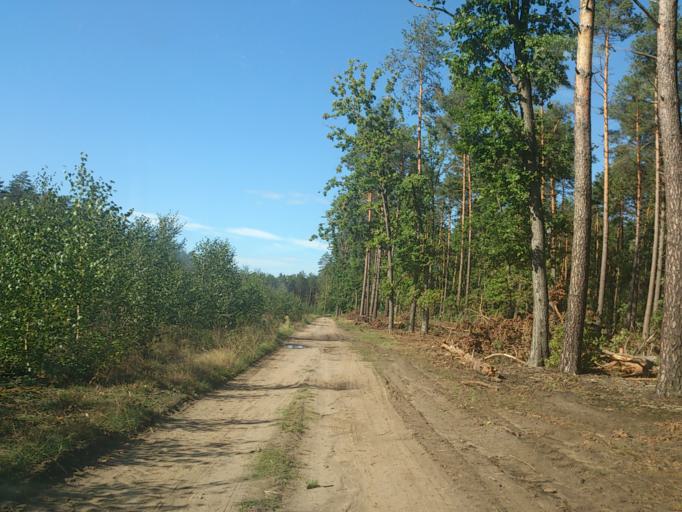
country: PL
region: Kujawsko-Pomorskie
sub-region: Powiat golubsko-dobrzynski
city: Radomin
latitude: 53.1363
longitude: 19.1479
